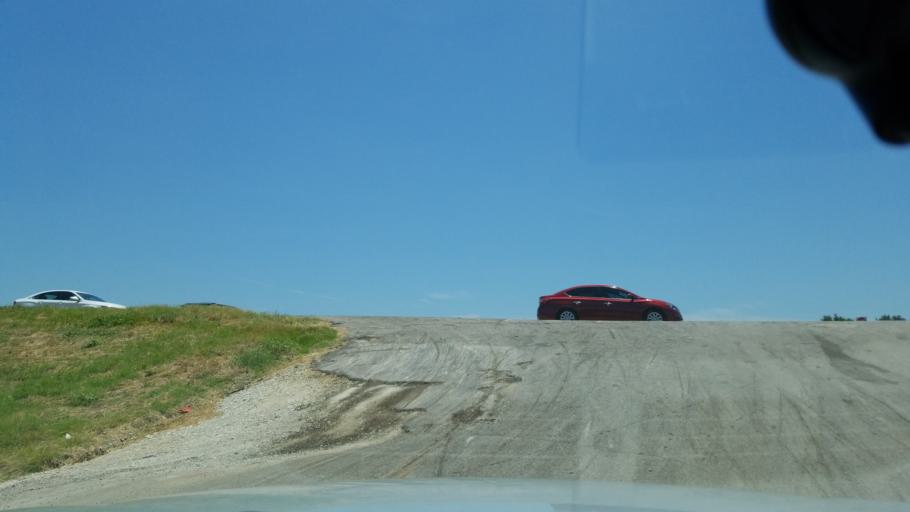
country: US
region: Texas
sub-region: Dallas County
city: Grand Prairie
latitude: 32.7492
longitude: -96.9448
